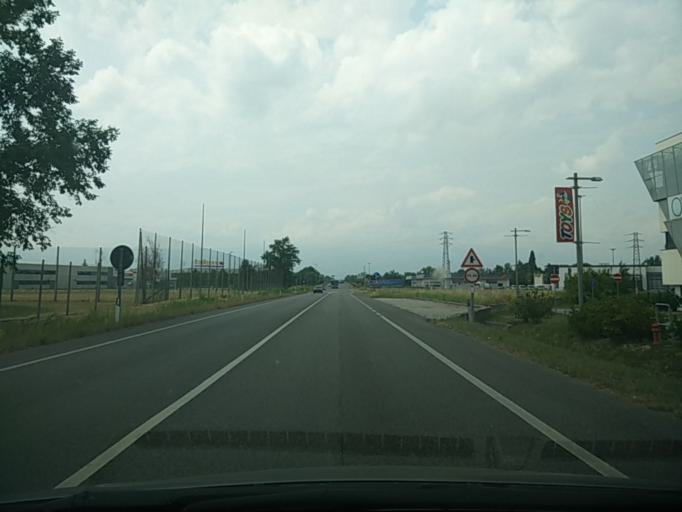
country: IT
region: Friuli Venezia Giulia
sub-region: Provincia di Pordenone
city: Pordenone
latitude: 45.9522
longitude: 12.6876
